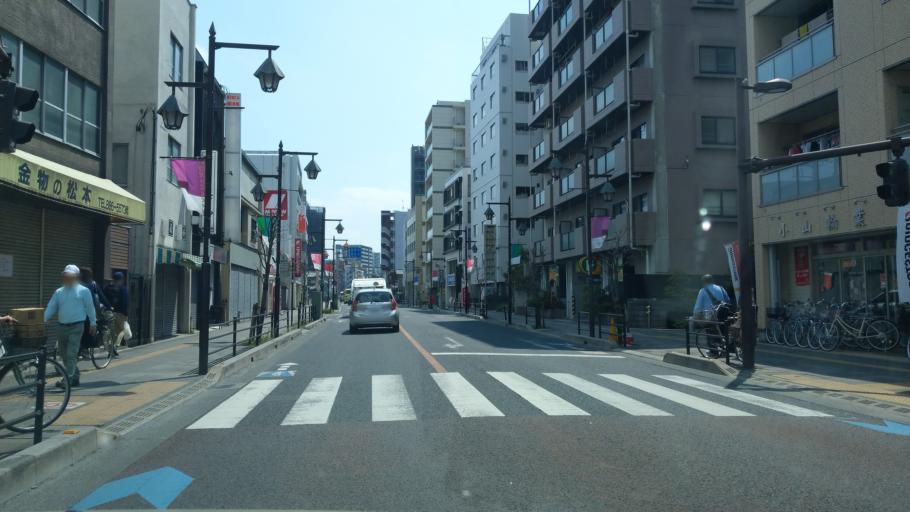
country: JP
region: Saitama
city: Yono
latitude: 35.8715
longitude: 139.6478
